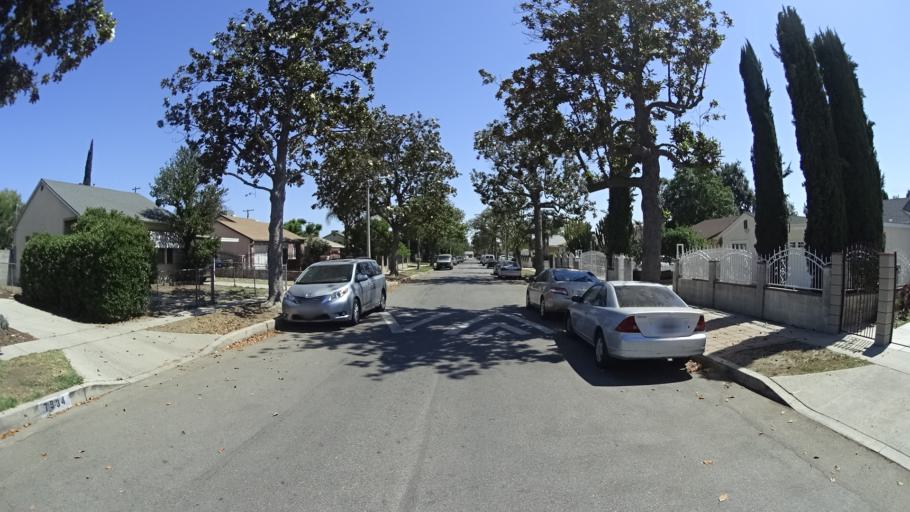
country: US
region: California
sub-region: Los Angeles County
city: Van Nuys
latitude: 34.2151
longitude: -118.4400
